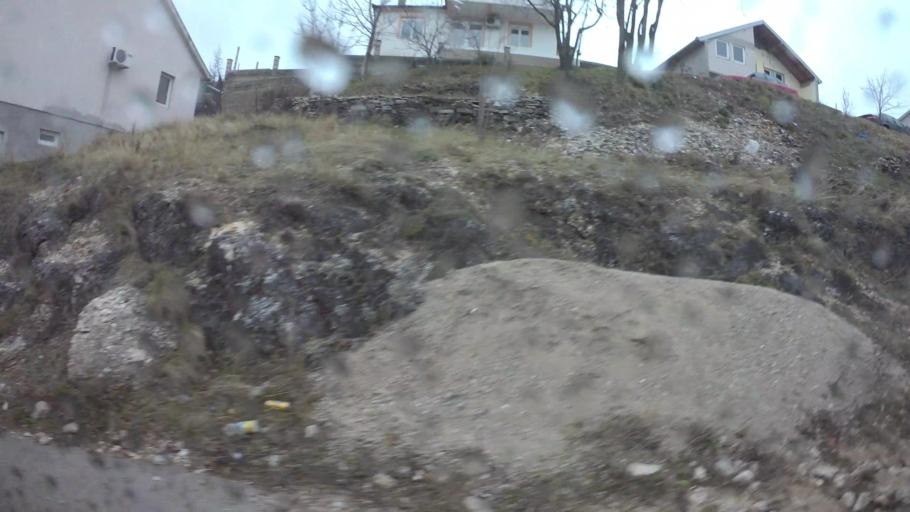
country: BA
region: Federation of Bosnia and Herzegovina
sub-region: Hercegovacko-Bosanski Kanton
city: Mostar
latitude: 43.3532
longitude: 17.8180
